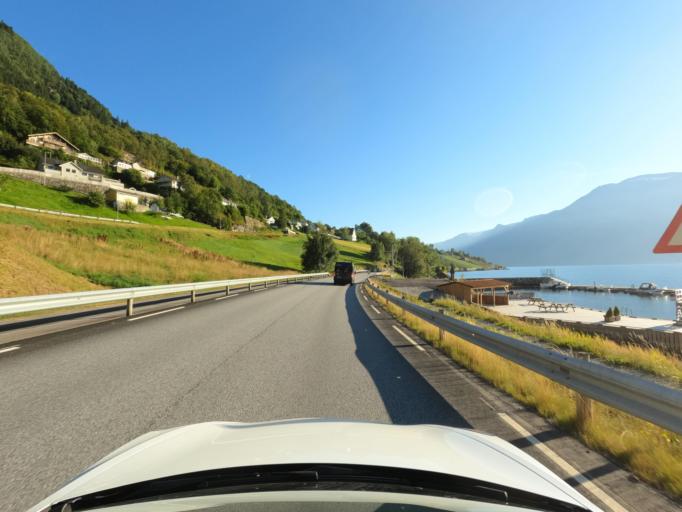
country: NO
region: Hordaland
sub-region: Ullensvang
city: Kinsarvik
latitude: 60.2595
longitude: 6.6234
